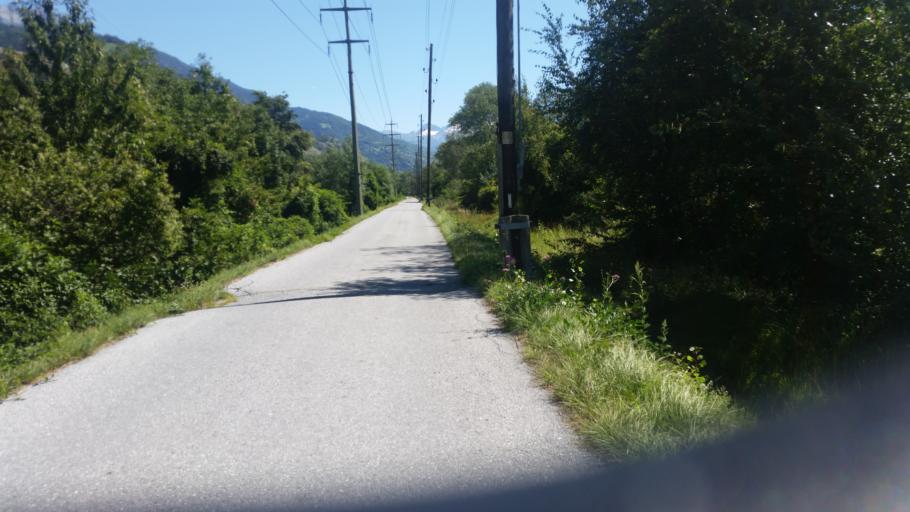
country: CH
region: Valais
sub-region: Raron District
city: Raron
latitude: 46.3073
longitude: 7.8042
